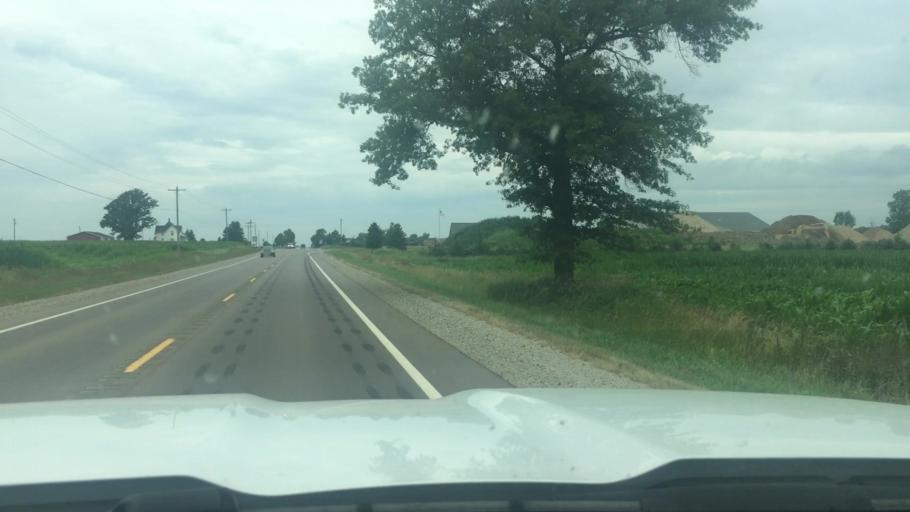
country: US
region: Michigan
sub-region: Clinton County
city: Fowler
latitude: 43.0017
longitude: -84.6959
